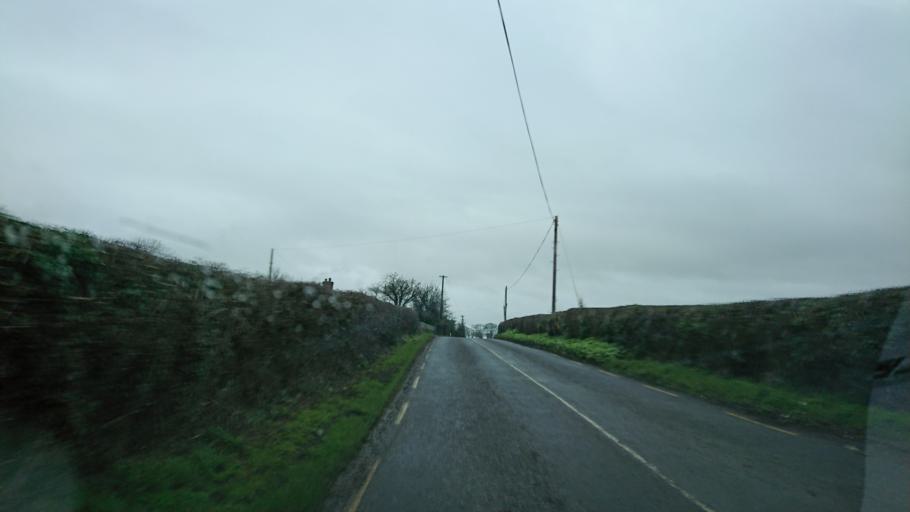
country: IE
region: Leinster
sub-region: Kilkenny
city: Callan
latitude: 52.5292
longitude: -7.2984
